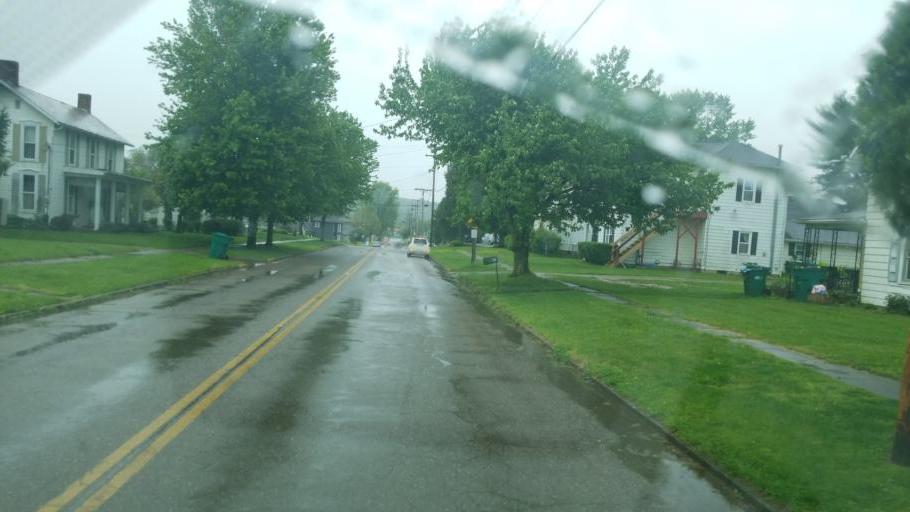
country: US
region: Ohio
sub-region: Muskingum County
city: Frazeysburg
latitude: 40.1208
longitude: -82.1168
